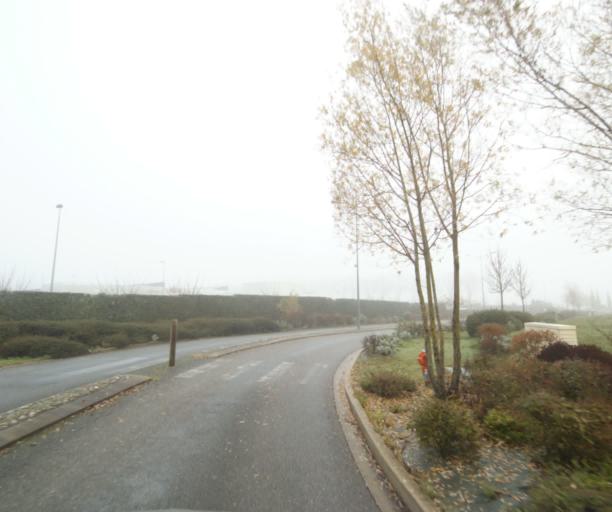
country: FR
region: Midi-Pyrenees
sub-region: Departement de la Haute-Garonne
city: Villemur-sur-Tarn
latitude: 43.8400
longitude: 1.4974
